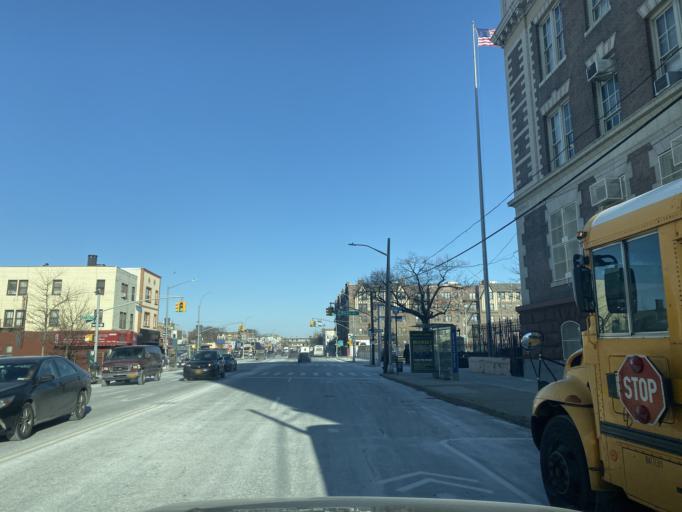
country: US
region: New York
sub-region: Bronx
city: The Bronx
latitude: 40.8294
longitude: -73.8504
